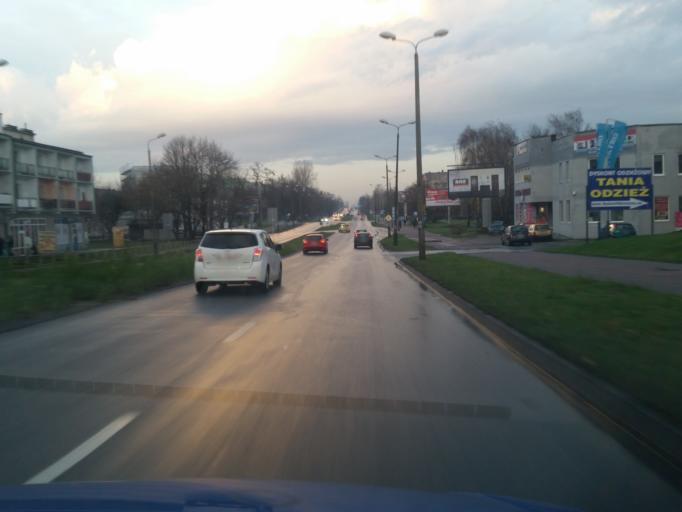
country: PL
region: Silesian Voivodeship
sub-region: Dabrowa Gornicza
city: Dabrowa Gornicza
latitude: 50.3052
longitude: 19.1893
